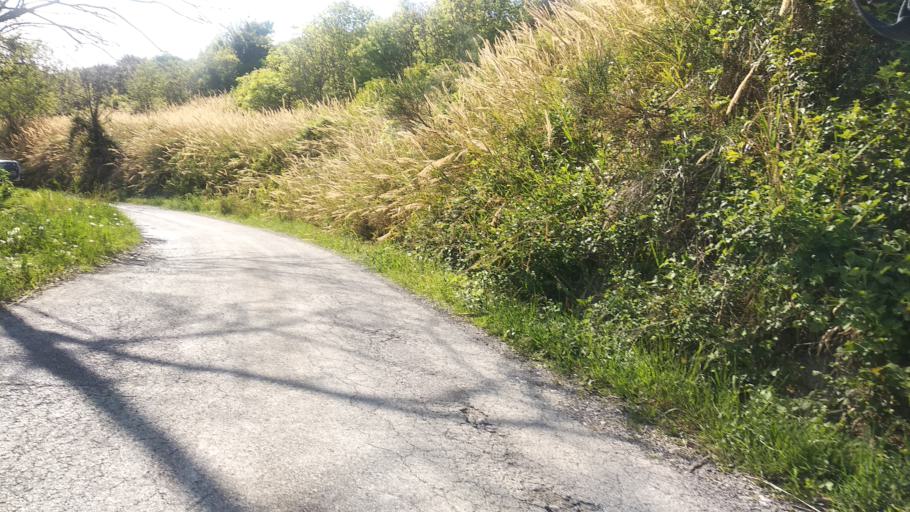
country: IT
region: Emilia-Romagna
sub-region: Provincia di Ravenna
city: Fognano
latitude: 44.2235
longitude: 11.7301
